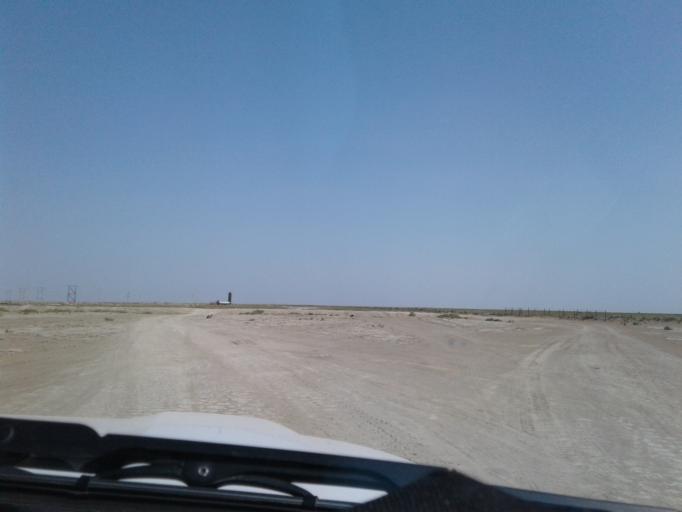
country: IR
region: Golestan
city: Gomishan
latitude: 37.8159
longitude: 53.9218
